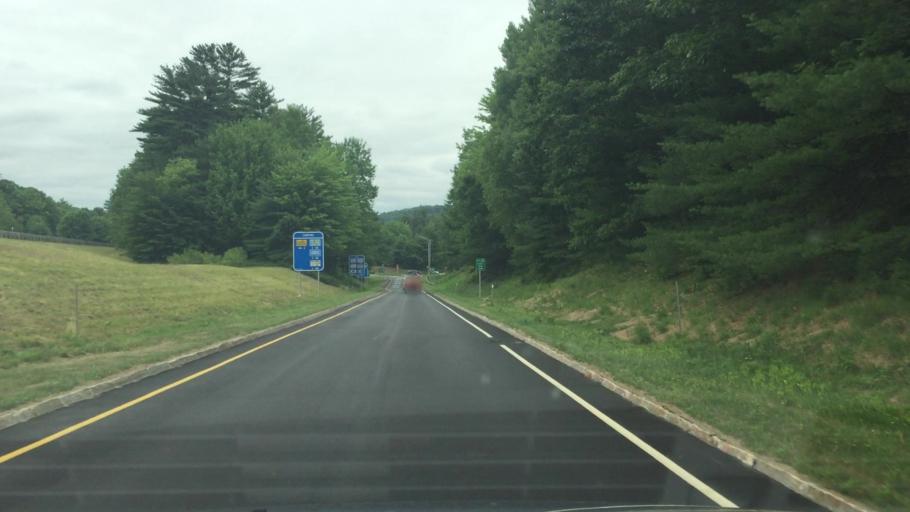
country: US
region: New Hampshire
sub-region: Grafton County
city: Ashland
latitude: 43.6113
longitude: -71.6409
